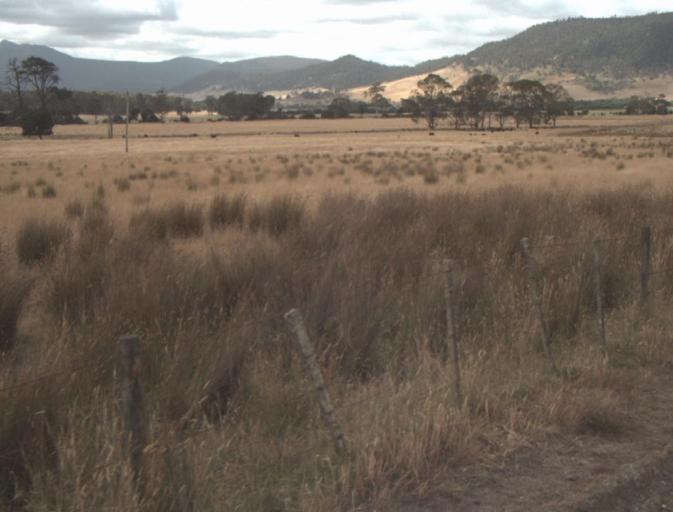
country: AU
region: Tasmania
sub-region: Northern Midlands
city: Evandale
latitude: -41.4714
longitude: 147.4466
